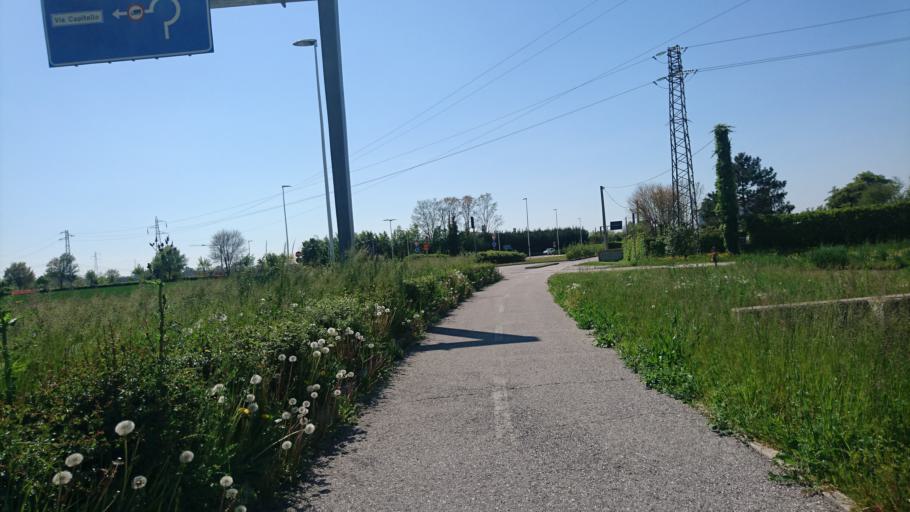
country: IT
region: Veneto
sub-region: Provincia di Treviso
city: Conscio
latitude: 45.6010
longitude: 12.2797
